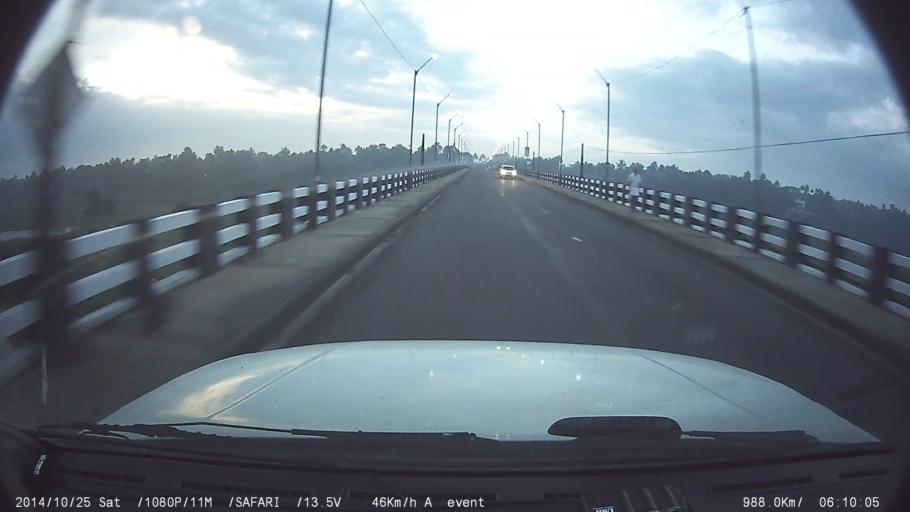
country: IN
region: Kerala
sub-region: Ernakulam
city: Angamali
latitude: 10.1636
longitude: 76.4407
